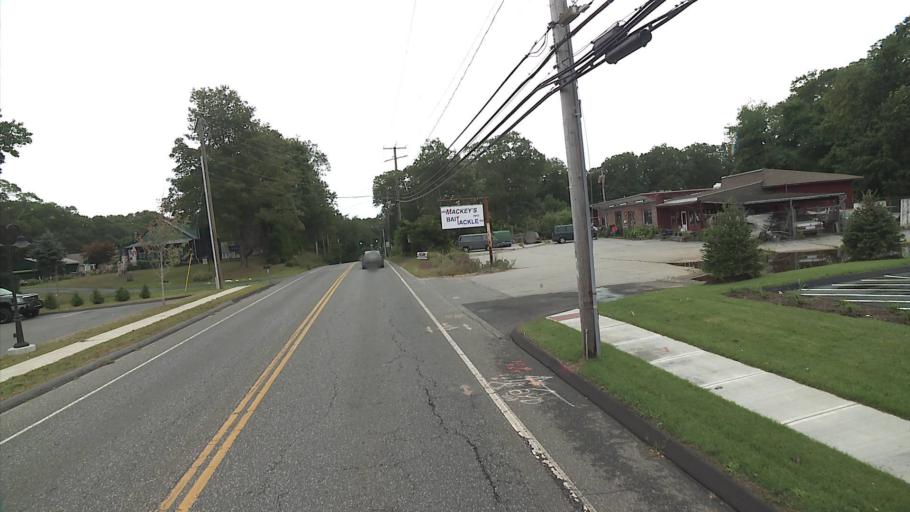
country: US
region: Connecticut
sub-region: New London County
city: Niantic
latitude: 41.3184
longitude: -72.2256
